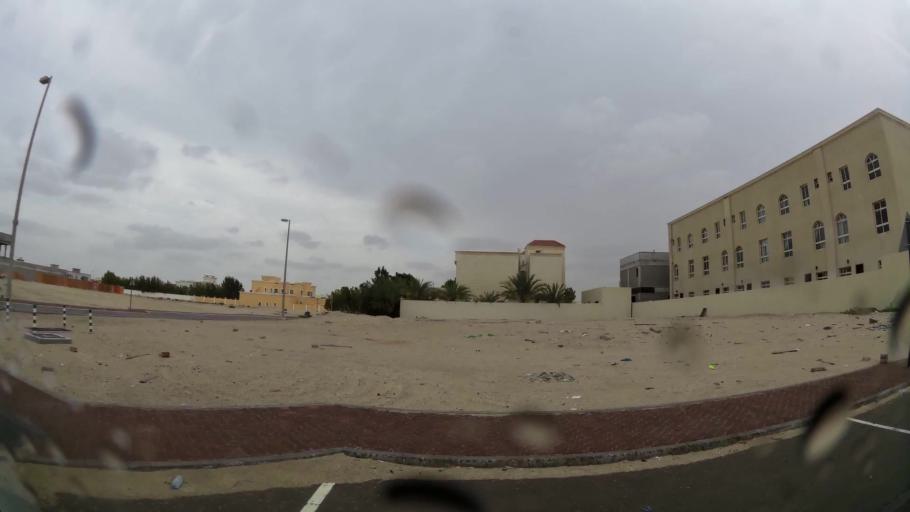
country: AE
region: Abu Dhabi
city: Abu Dhabi
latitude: 24.3614
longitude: 54.6425
